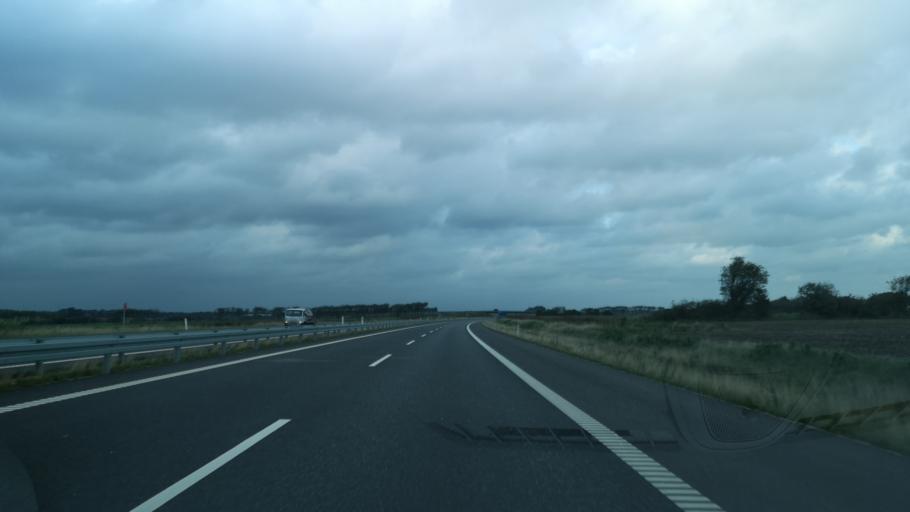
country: DK
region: Central Jutland
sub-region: Herning Kommune
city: Snejbjerg
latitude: 56.1412
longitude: 8.8696
